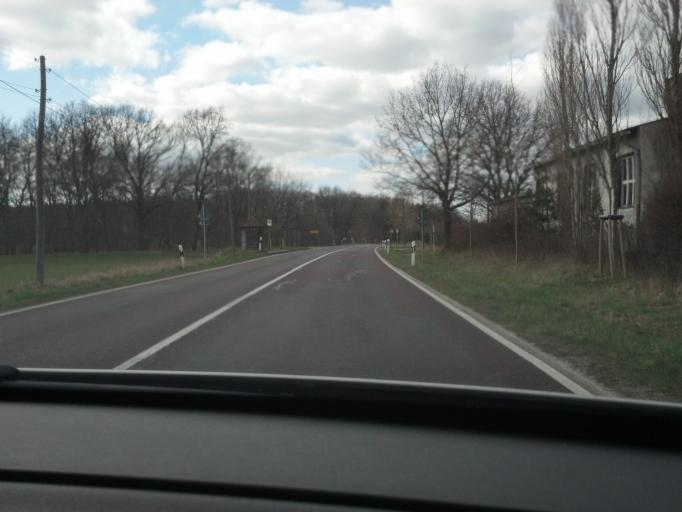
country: DE
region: Mecklenburg-Vorpommern
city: Robel
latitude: 53.3341
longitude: 12.5478
